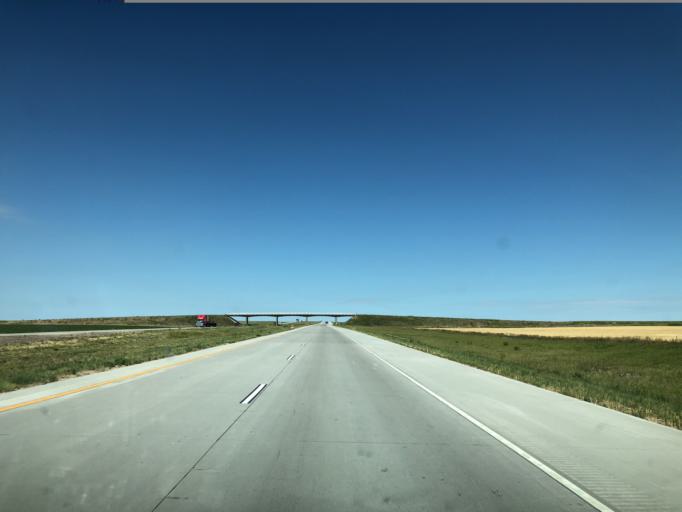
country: US
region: Colorado
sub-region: Kit Carson County
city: Burlington
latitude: 39.2942
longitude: -102.7762
